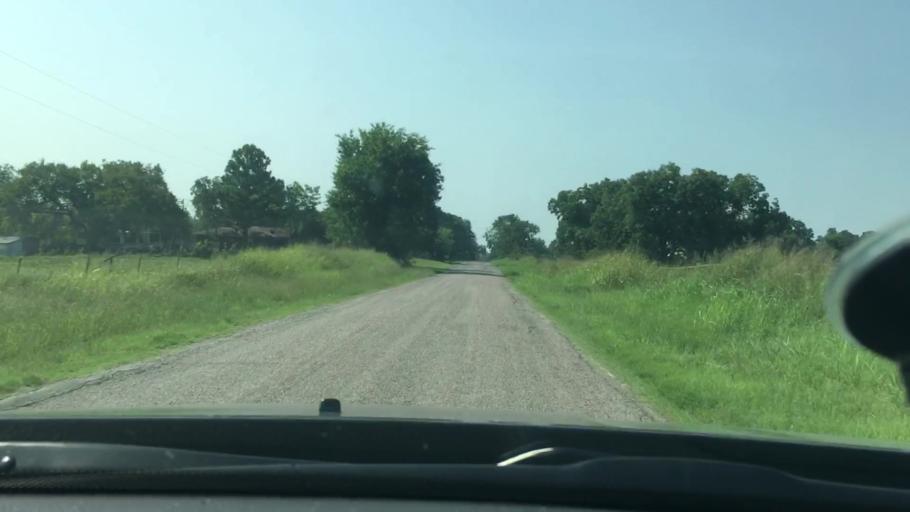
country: US
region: Oklahoma
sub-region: Pontotoc County
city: Ada
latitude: 34.6670
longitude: -96.5298
